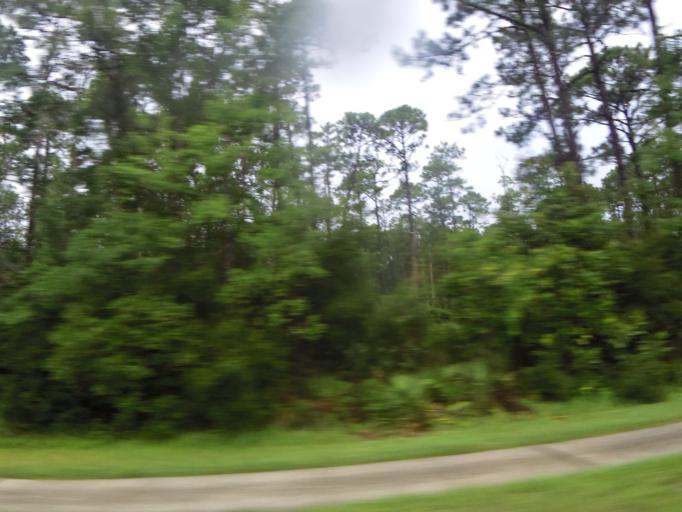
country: US
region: Florida
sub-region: Duval County
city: Jacksonville Beach
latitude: 30.2694
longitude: -81.5101
